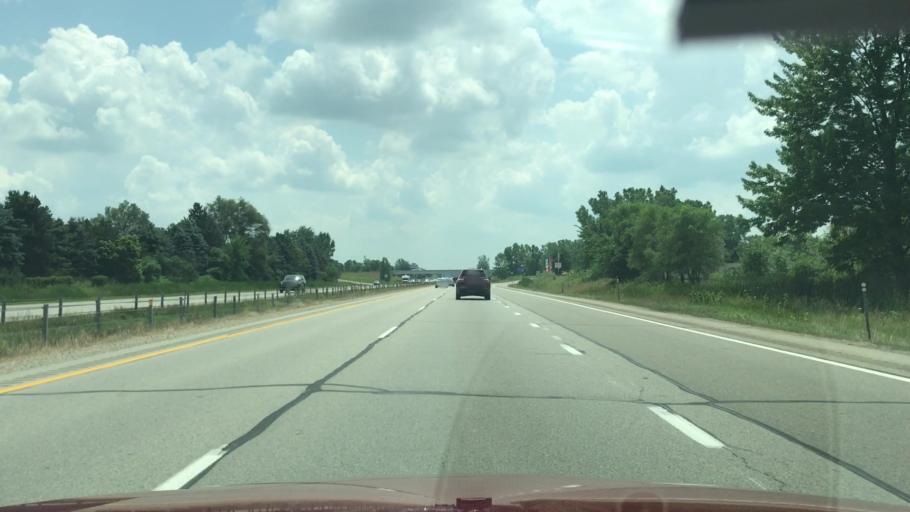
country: US
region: Michigan
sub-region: Allegan County
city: Wayland
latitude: 42.6782
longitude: -85.6611
